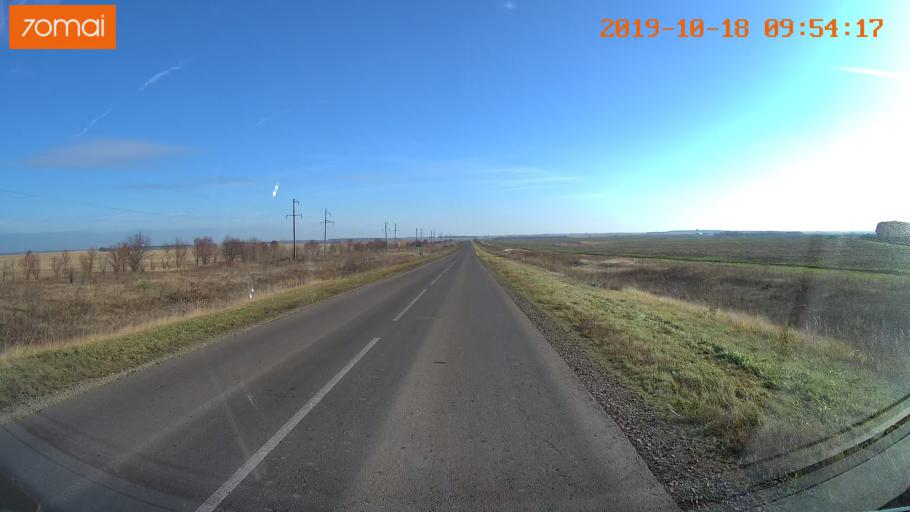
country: RU
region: Tula
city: Kazachka
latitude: 53.3645
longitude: 38.3411
